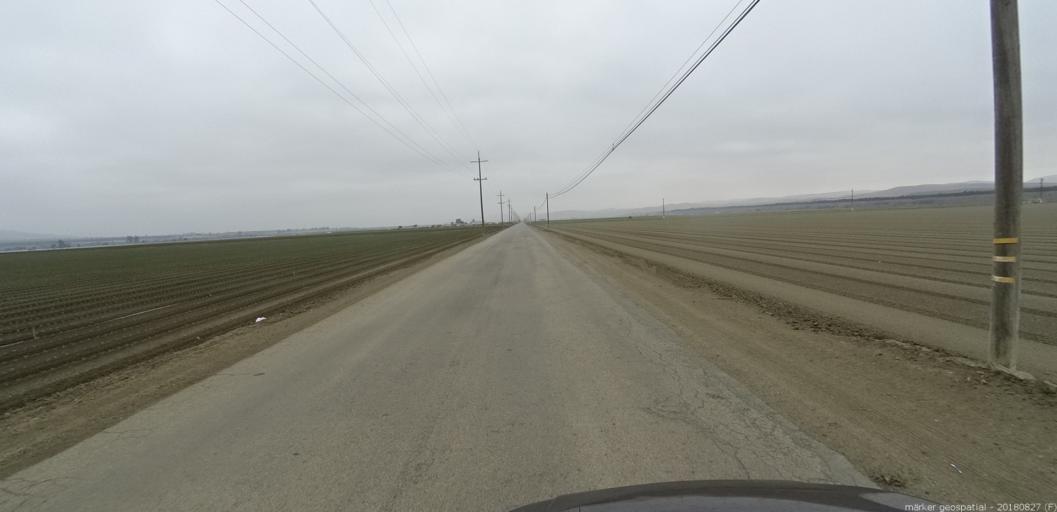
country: US
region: California
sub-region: Monterey County
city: King City
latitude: 36.2306
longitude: -121.1412
